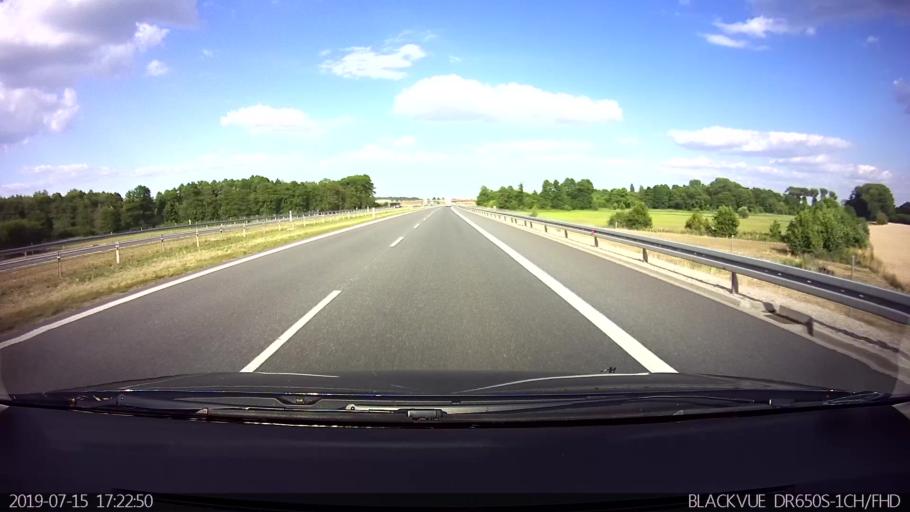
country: PL
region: Greater Poland Voivodeship
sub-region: Powiat kepinski
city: Kepno
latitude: 51.3168
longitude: 17.9685
